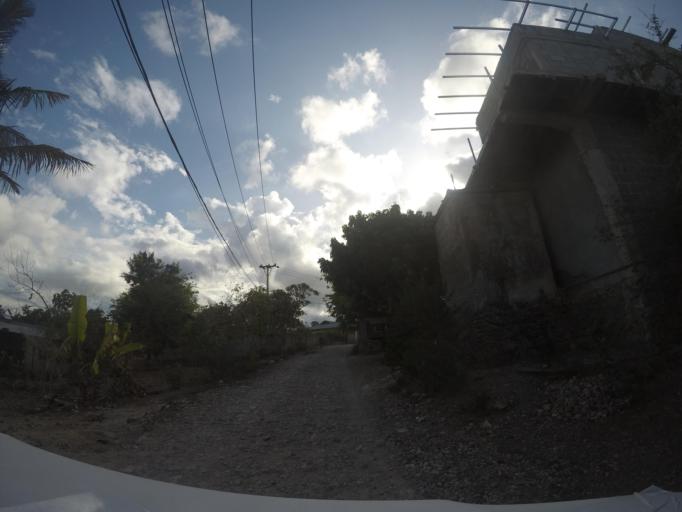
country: TL
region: Baucau
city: Baucau
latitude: -8.4759
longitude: 126.4593
